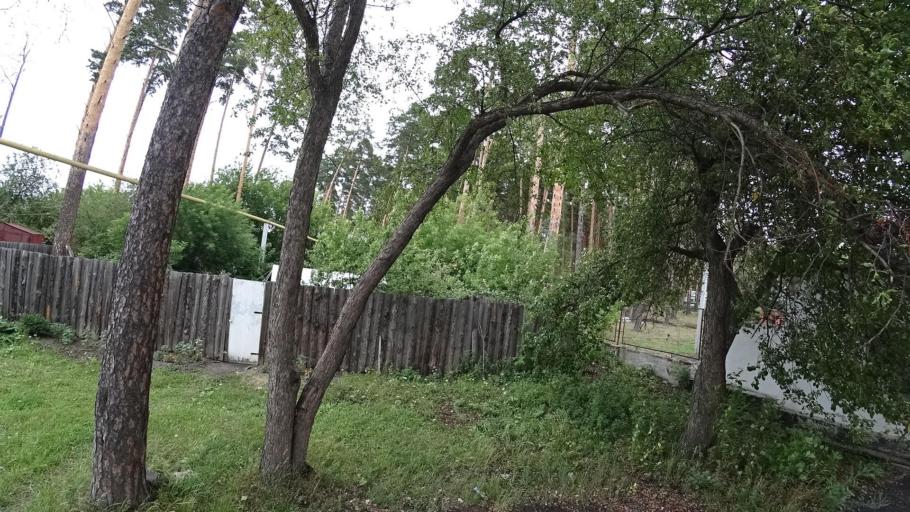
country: RU
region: Sverdlovsk
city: Kamyshlov
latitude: 56.8403
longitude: 62.7433
